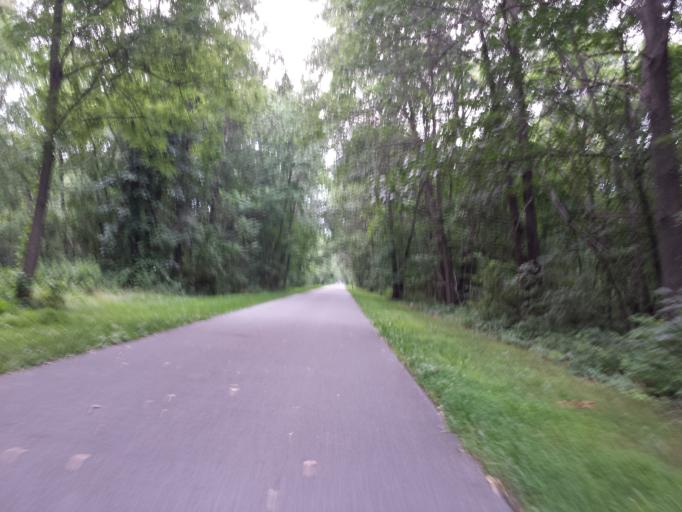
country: US
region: New York
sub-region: Dutchess County
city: Arlington
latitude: 41.7106
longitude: -73.8911
